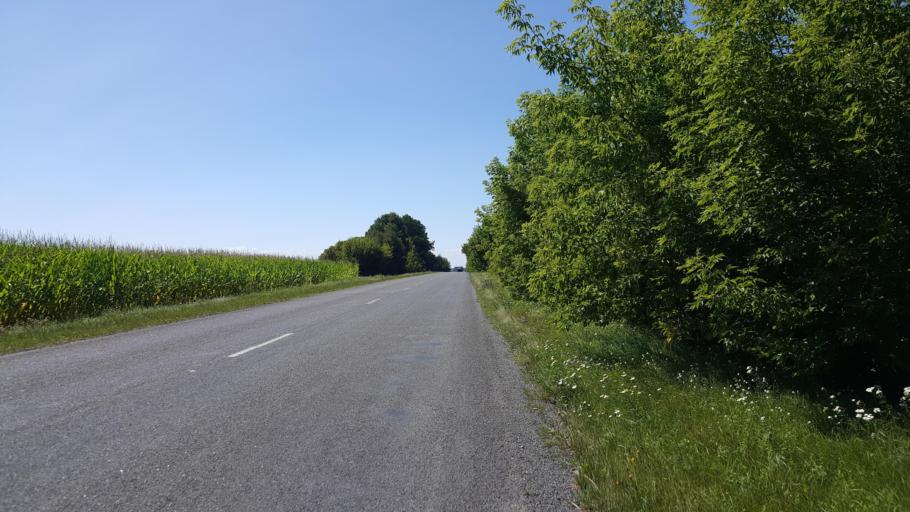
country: BY
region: Brest
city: Charnawchytsy
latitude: 52.2062
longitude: 23.8057
